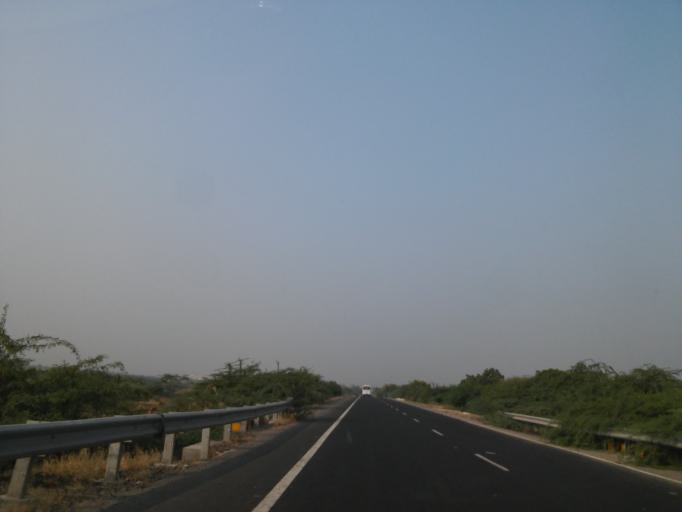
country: IN
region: Gujarat
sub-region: Kachchh
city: Anjar
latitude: 23.2908
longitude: 70.0288
